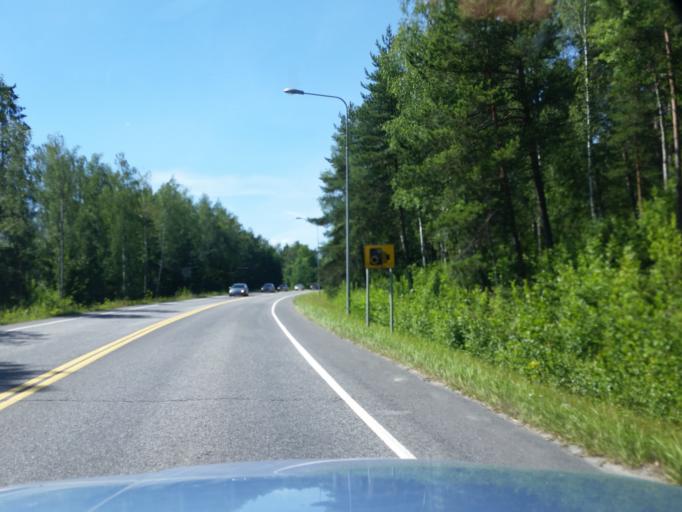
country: FI
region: Varsinais-Suomi
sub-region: Aboland-Turunmaa
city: Pargas
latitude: 60.3154
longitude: 22.3310
